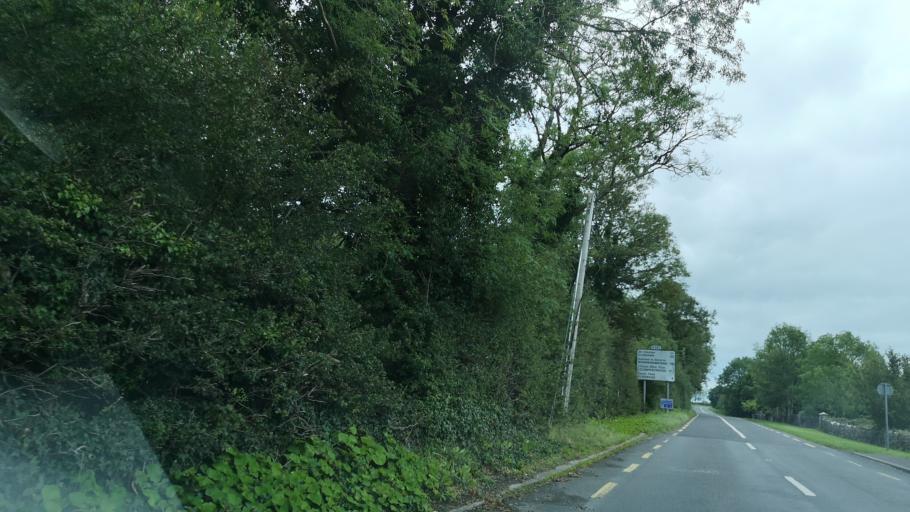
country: IE
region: Connaught
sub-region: County Galway
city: Ballinasloe
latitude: 53.3197
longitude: -8.1793
